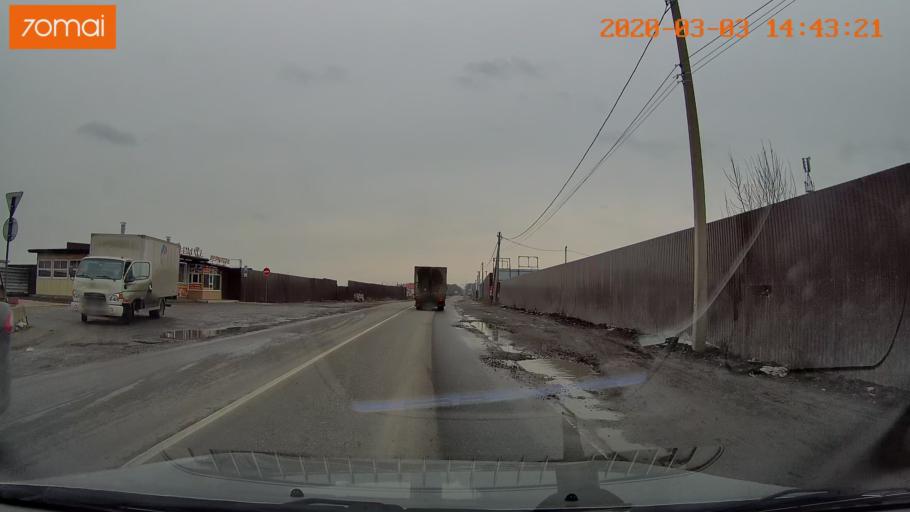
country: RU
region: Moskovskaya
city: Korenevo
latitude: 55.7014
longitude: 38.0186
